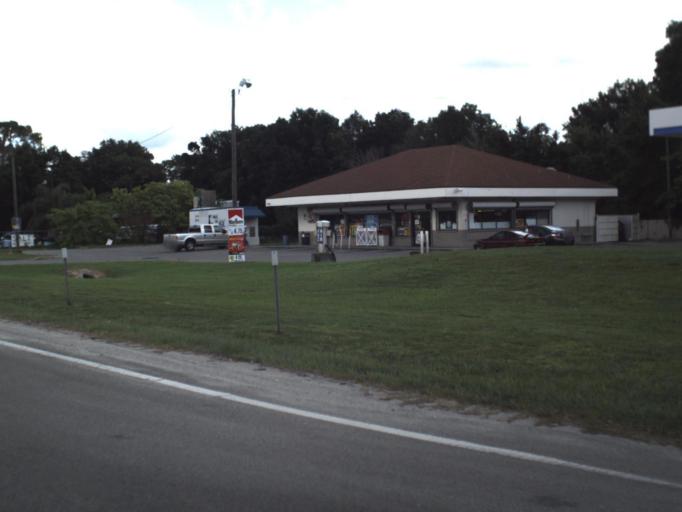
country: US
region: Florida
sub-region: Polk County
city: Kathleen
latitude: 28.1931
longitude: -82.0009
